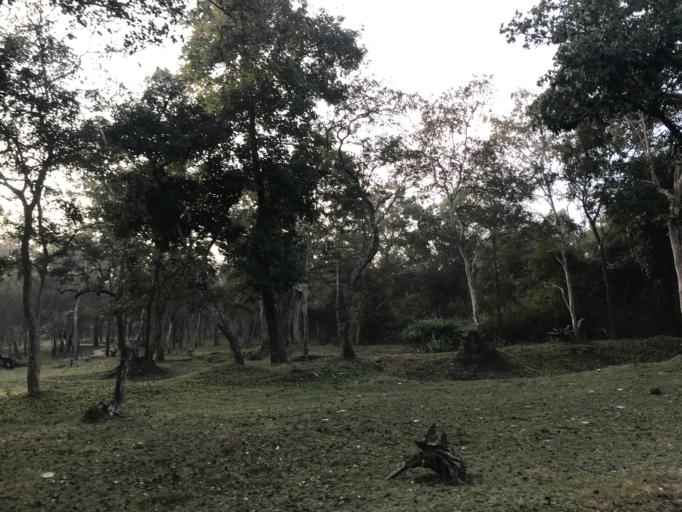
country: IN
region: Karnataka
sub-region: Mysore
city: Heggadadevankote
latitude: 12.0069
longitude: 76.2365
